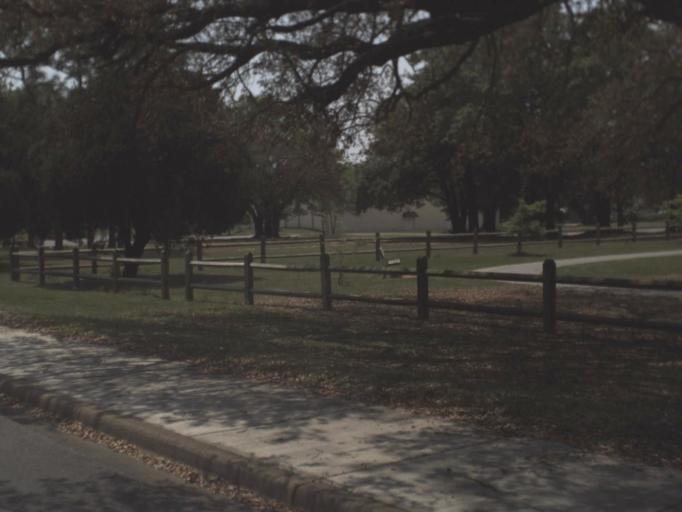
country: US
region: Florida
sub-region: Escambia County
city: Brent
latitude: 30.4641
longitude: -87.2415
